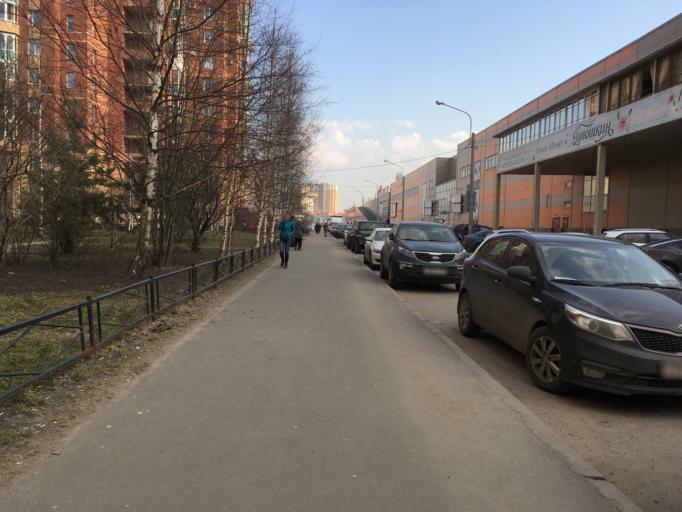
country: RU
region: St.-Petersburg
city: Komendantsky aerodrom
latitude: 60.0052
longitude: 30.2633
